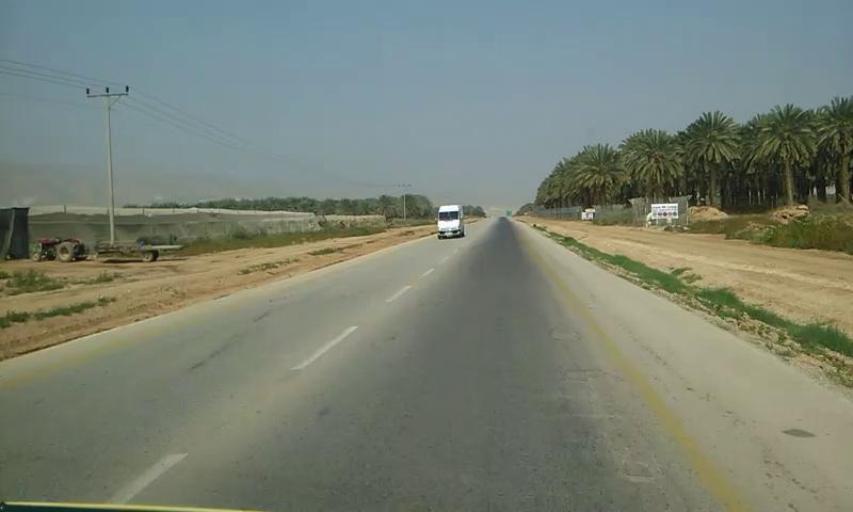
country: PS
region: West Bank
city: Al Fasayil
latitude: 31.9933
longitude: 35.4579
